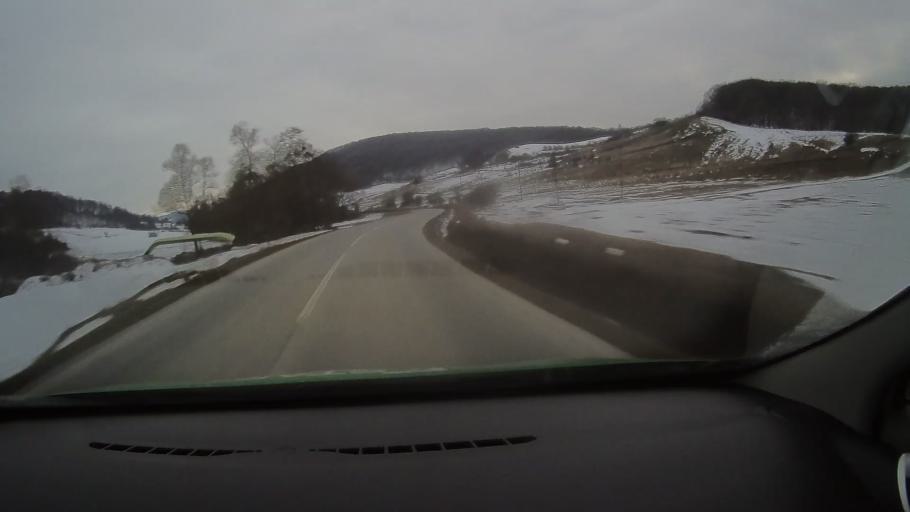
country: RO
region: Harghita
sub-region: Comuna Mugeni
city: Mugeni
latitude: 46.2301
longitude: 25.2398
